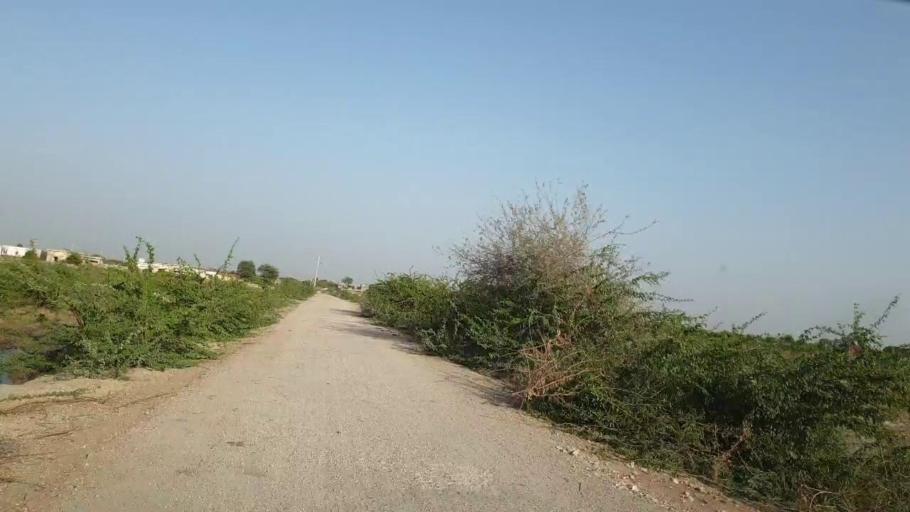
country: PK
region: Sindh
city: Kunri
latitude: 25.0735
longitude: 69.4525
